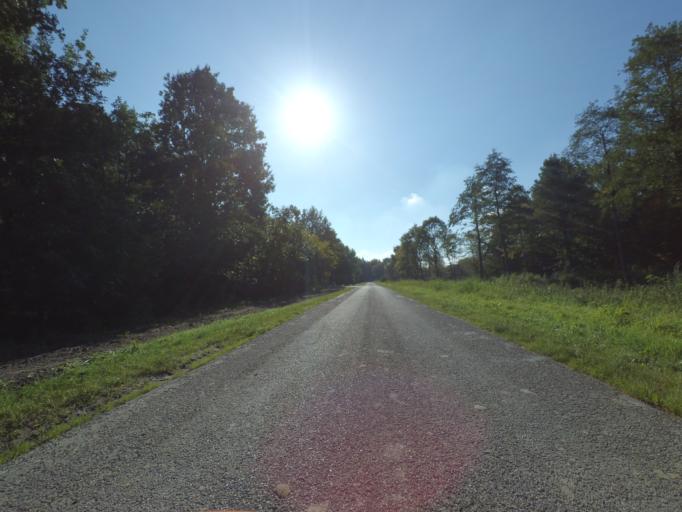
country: NL
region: Flevoland
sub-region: Gemeente Zeewolde
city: Zeewolde
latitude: 52.3055
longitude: 5.5271
